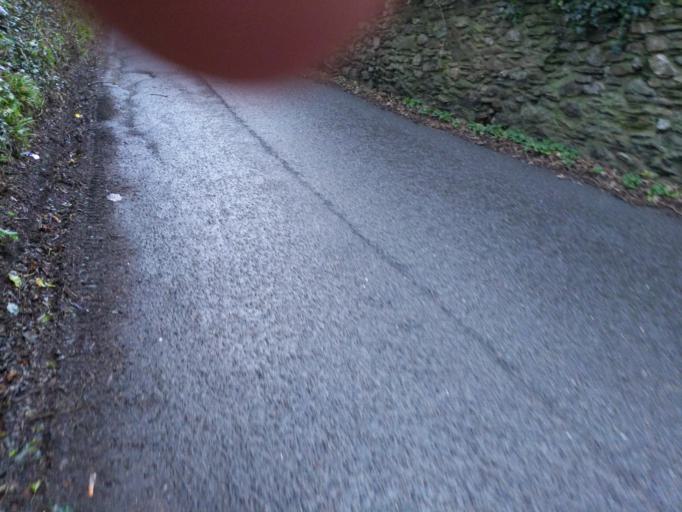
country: GB
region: England
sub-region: Devon
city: Wembury
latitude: 50.3155
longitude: -4.0367
